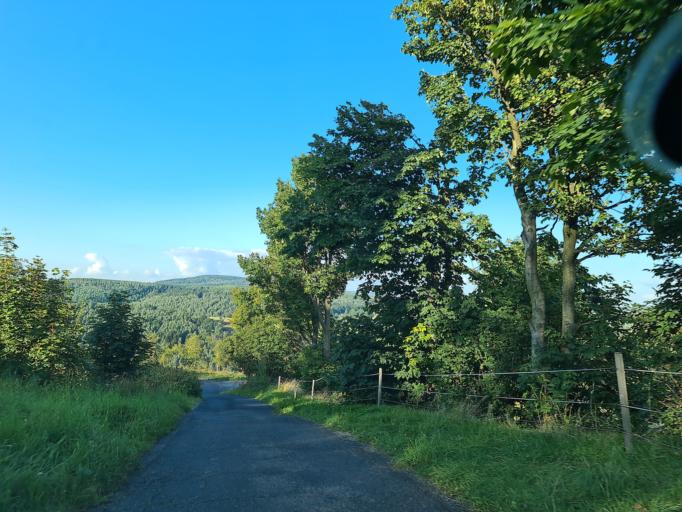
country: DE
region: Saxony
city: Deutschneudorf
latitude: 50.6033
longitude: 13.4433
